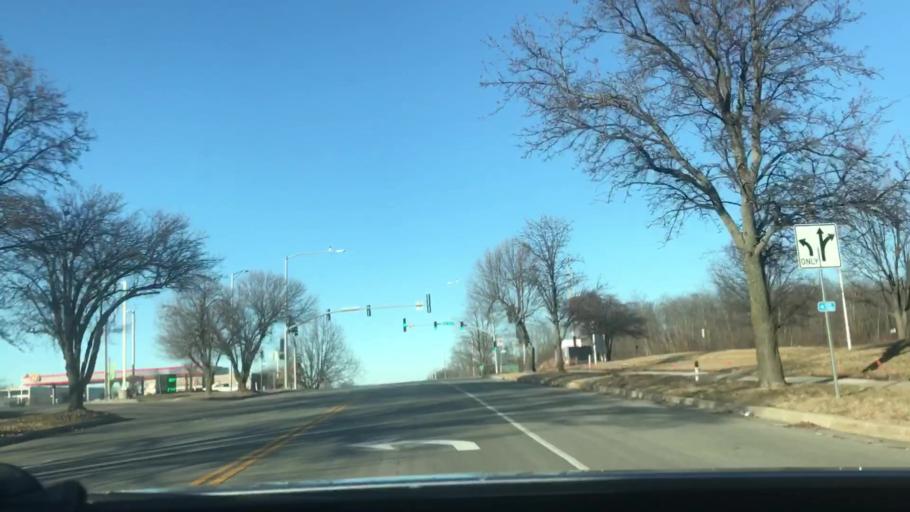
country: US
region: Missouri
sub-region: Platte County
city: Weatherby Lake
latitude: 39.2959
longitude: -94.6818
